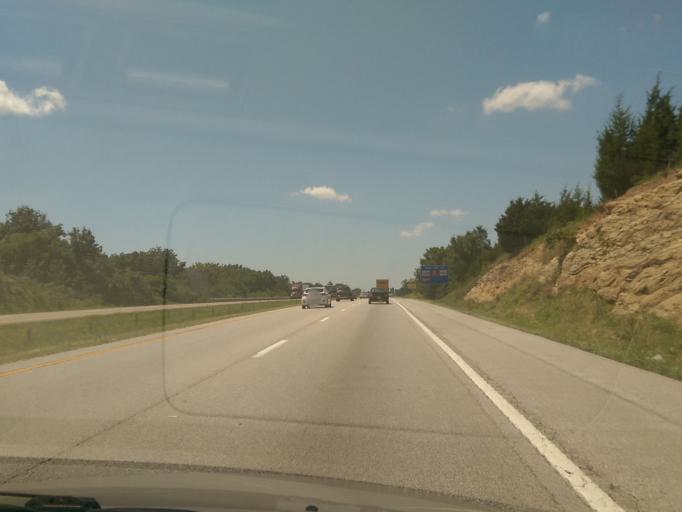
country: US
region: Missouri
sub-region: Cooper County
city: Boonville
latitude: 38.9361
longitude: -92.7630
